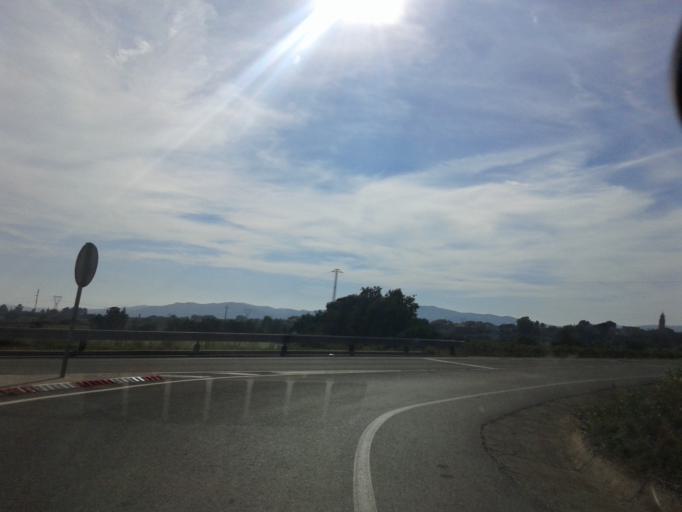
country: ES
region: Catalonia
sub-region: Provincia de Tarragona
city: Sant Jaume dels Domenys
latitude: 41.2856
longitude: 1.5604
